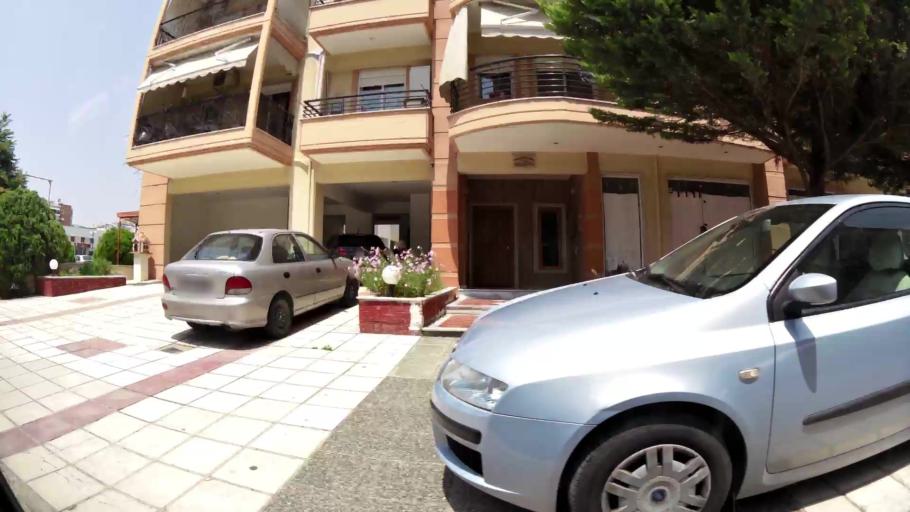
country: GR
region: Central Macedonia
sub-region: Nomos Thessalonikis
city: Evosmos
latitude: 40.6666
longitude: 22.9062
